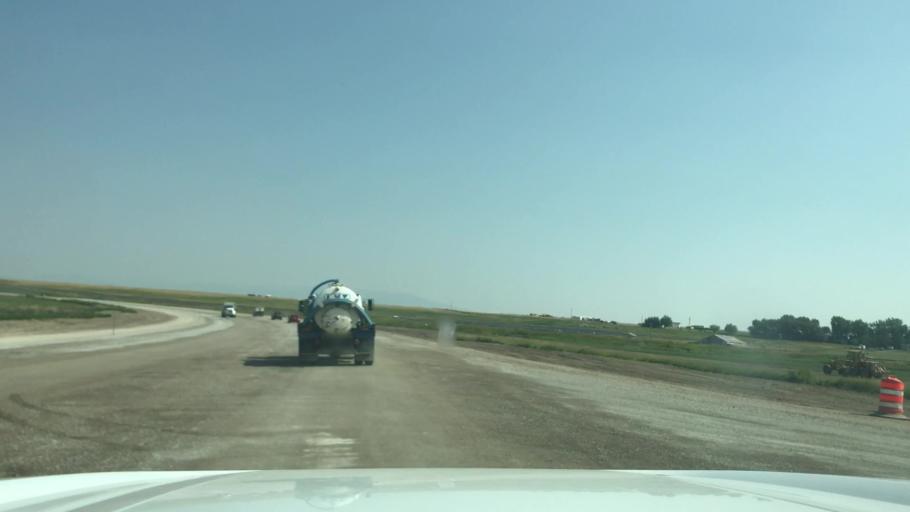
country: US
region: Montana
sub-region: Judith Basin County
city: Stanford
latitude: 47.0052
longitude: -109.8693
